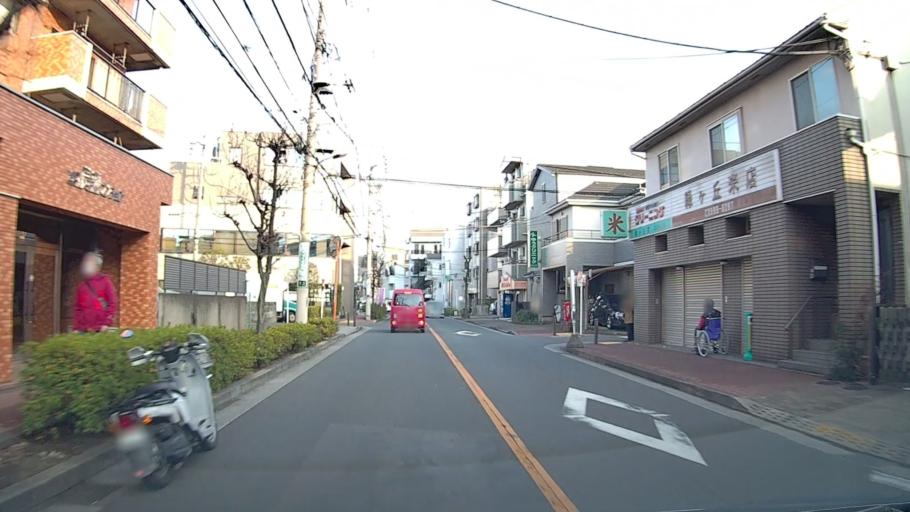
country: JP
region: Saitama
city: Wako
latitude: 35.7595
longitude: 139.6480
